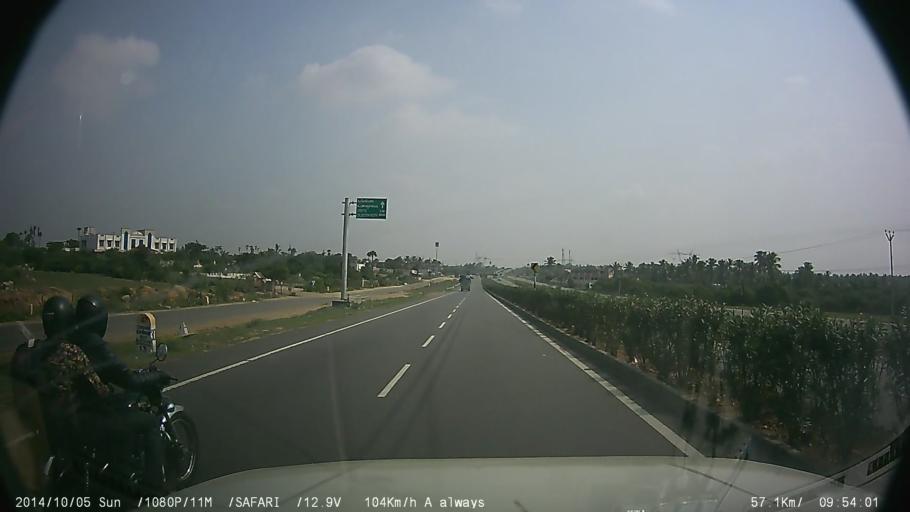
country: IN
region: Tamil Nadu
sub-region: Salem
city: Konganapuram
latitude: 11.4987
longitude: 77.9083
